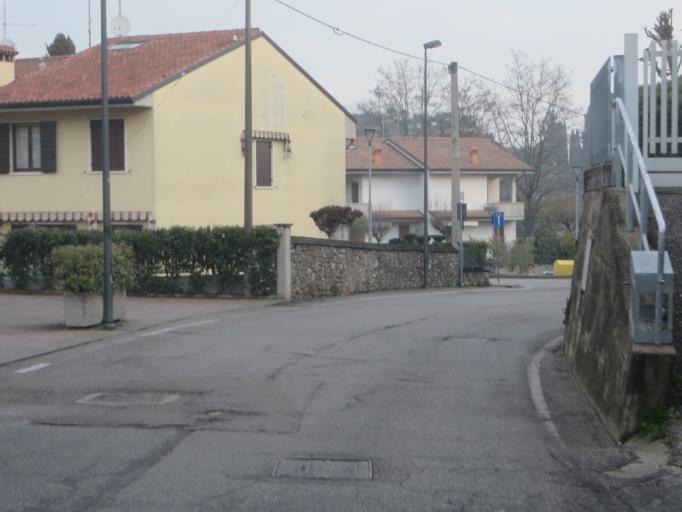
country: IT
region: Veneto
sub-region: Provincia di Verona
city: Sandra
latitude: 45.4556
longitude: 10.8176
